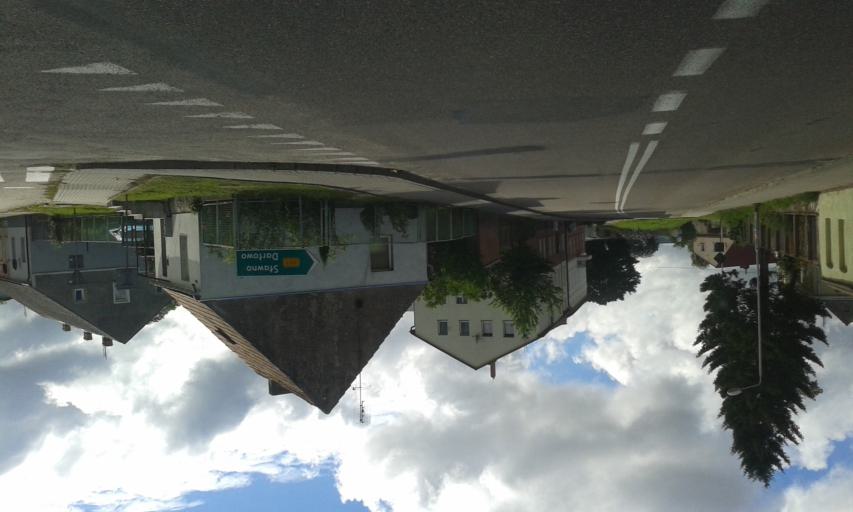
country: PL
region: West Pomeranian Voivodeship
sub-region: Powiat koszalinski
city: Bobolice
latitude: 53.9542
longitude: 16.5928
